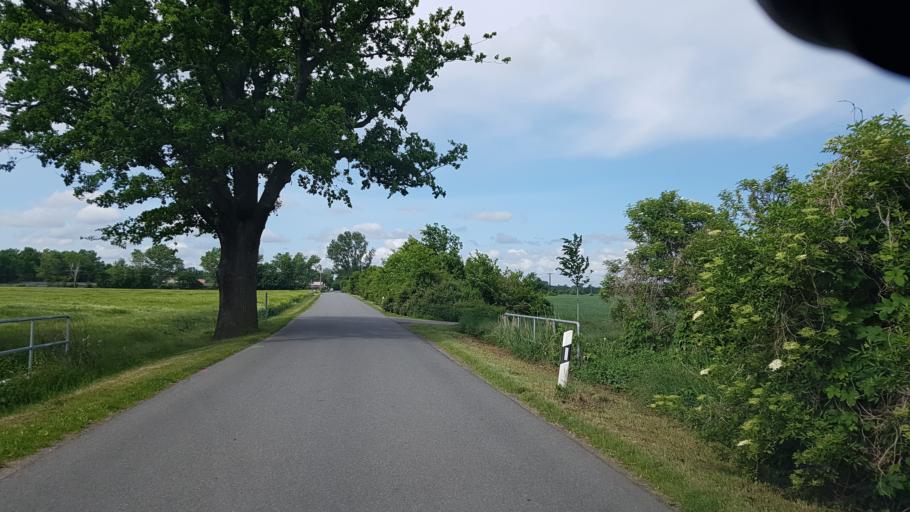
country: DE
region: Brandenburg
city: Luckau
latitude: 51.8358
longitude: 13.7493
